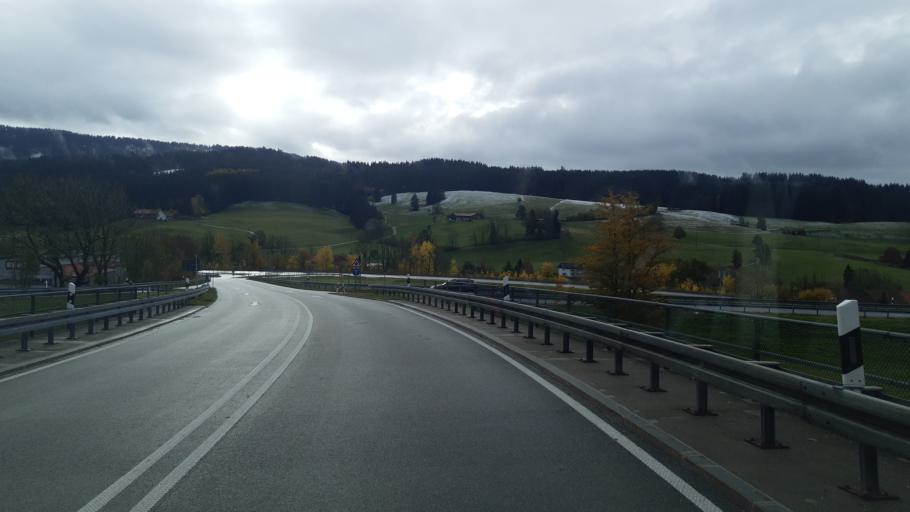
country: DE
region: Bavaria
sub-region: Swabia
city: Weitnau
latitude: 47.6429
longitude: 10.1103
